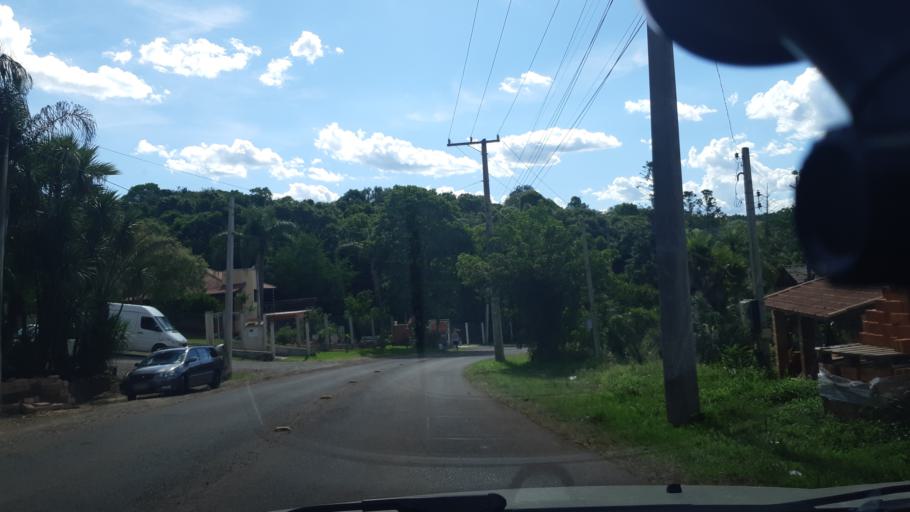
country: BR
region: Rio Grande do Sul
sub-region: Ivoti
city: Ivoti
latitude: -29.6209
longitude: -51.1140
